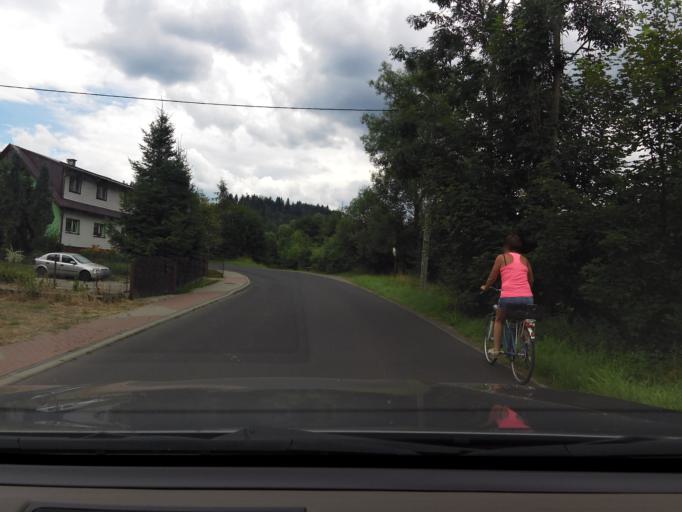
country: PL
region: Silesian Voivodeship
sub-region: Powiat zywiecki
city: Ujsoly
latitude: 49.4751
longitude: 19.1462
